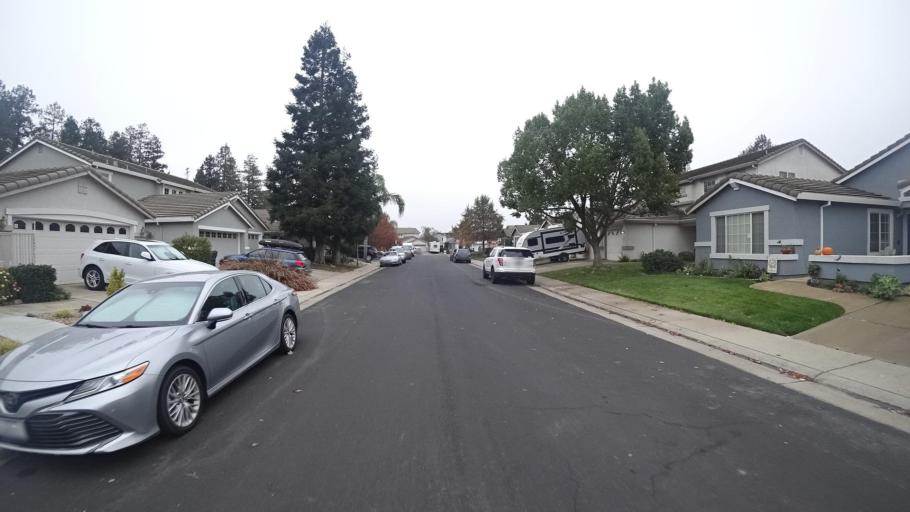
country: US
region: California
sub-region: Sacramento County
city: Elk Grove
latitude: 38.3941
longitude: -121.3653
